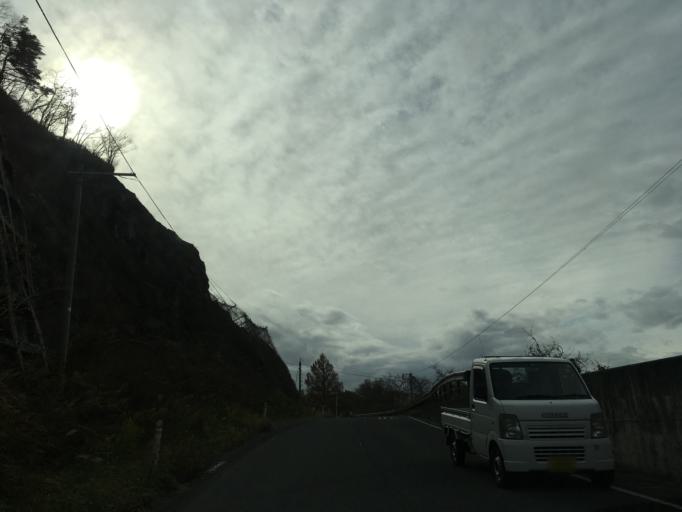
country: JP
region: Iwate
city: Ichinoseki
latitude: 38.7458
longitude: 141.2819
